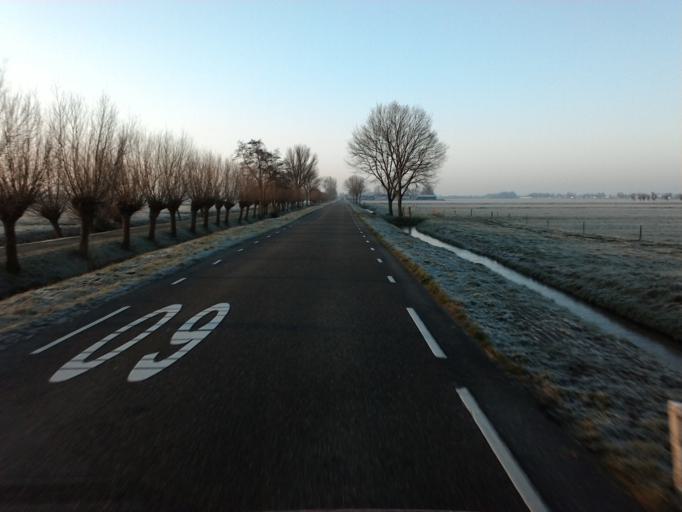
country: NL
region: South Holland
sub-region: Gemeente Gorinchem
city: Gorinchem
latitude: 51.8923
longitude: 4.9834
